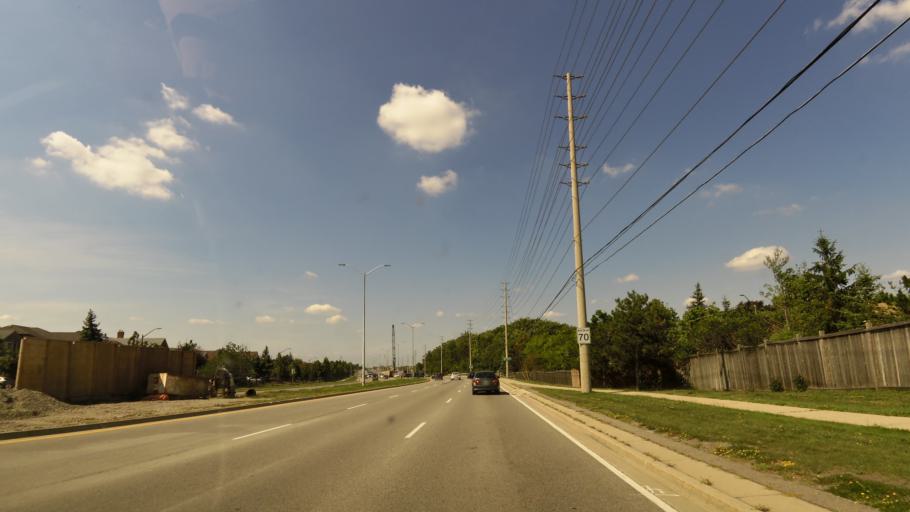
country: CA
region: Ontario
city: Mississauga
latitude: 43.5754
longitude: -79.7295
